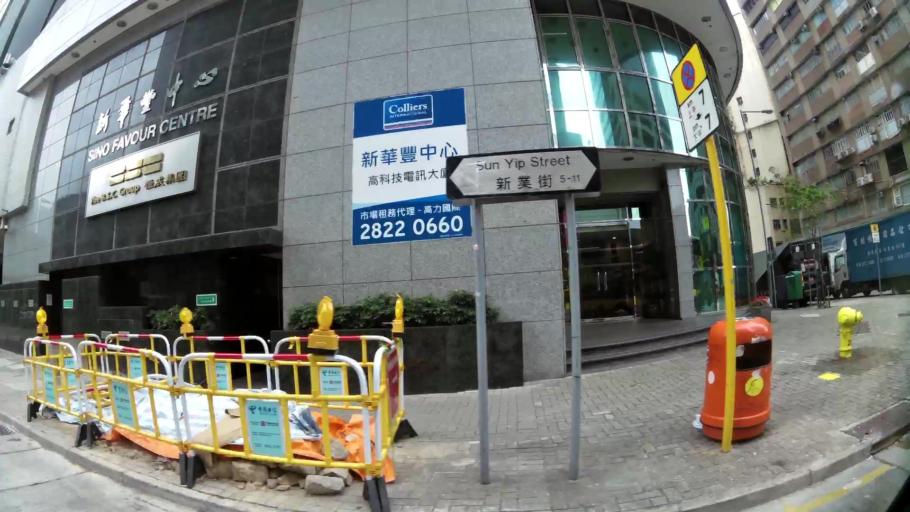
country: HK
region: Wanchai
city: Wan Chai
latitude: 22.2666
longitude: 114.2466
